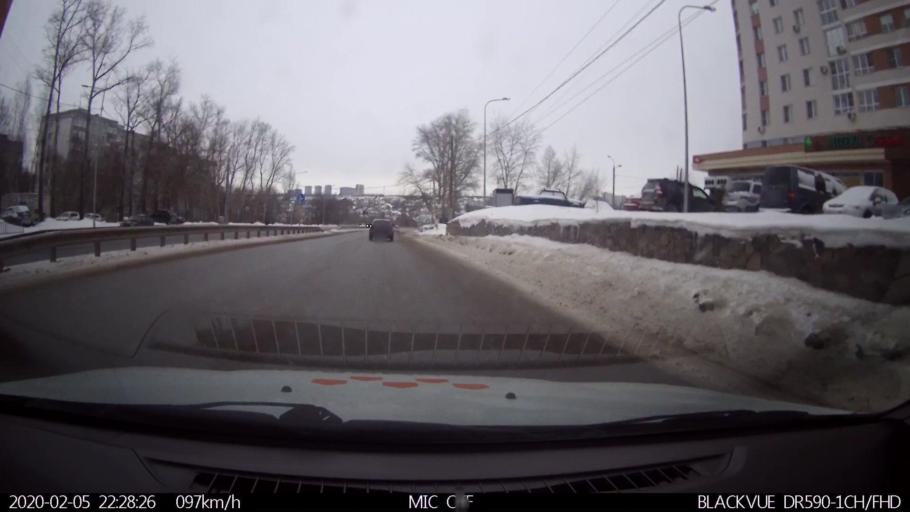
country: RU
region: Nizjnij Novgorod
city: Imeni Stepana Razina
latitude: 54.7575
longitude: 44.1332
